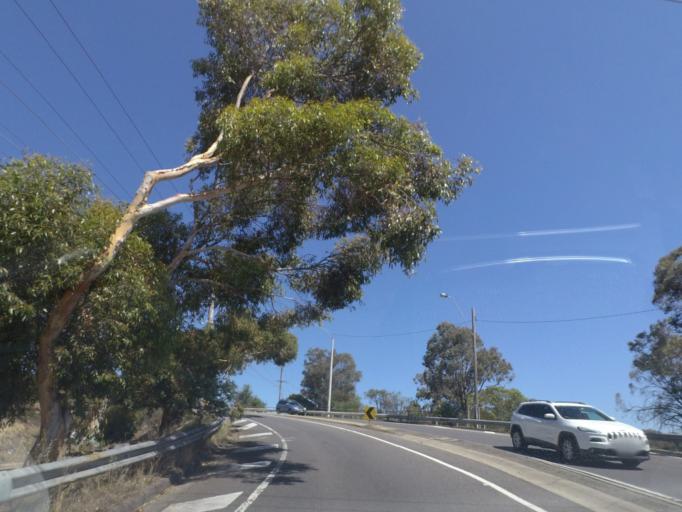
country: AU
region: Victoria
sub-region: Banyule
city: Montmorency
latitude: -37.7114
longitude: 145.1144
